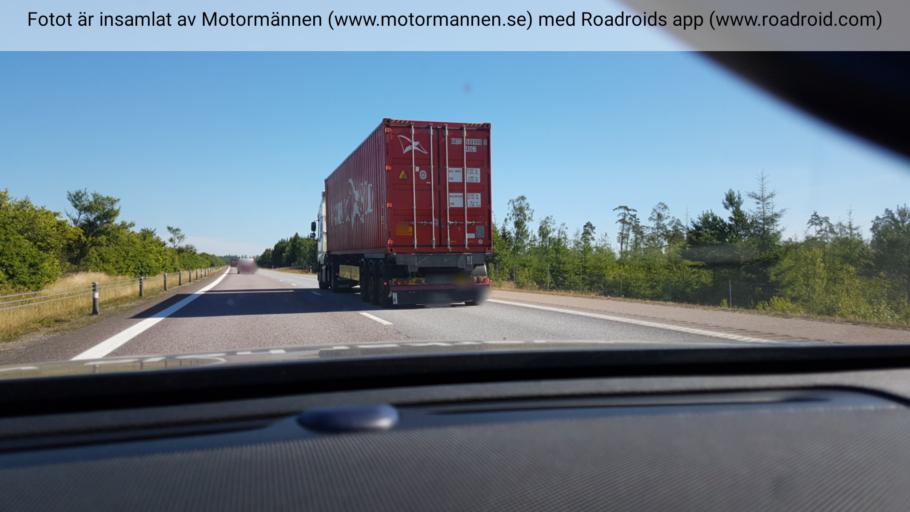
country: SE
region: Kronoberg
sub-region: Ljungby Kommun
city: Ljungby
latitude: 56.7297
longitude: 13.8489
